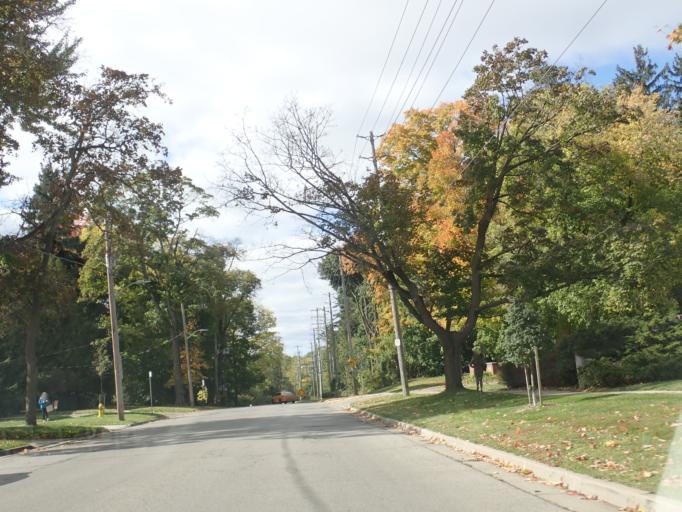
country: CA
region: Ontario
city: London
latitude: 42.9970
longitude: -81.2565
